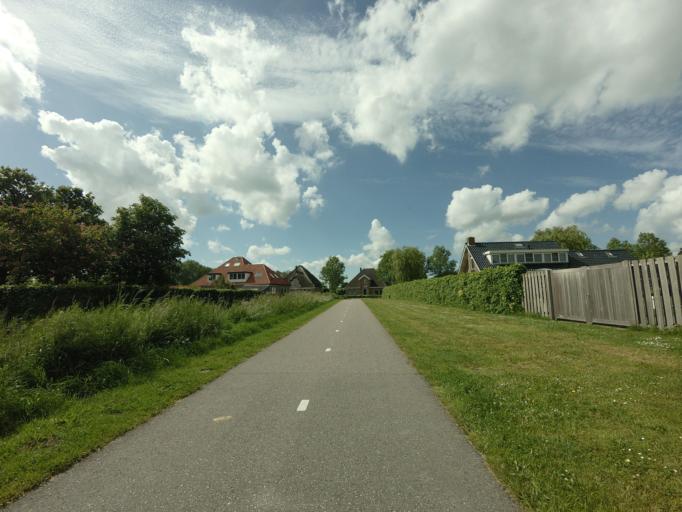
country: NL
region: North Holland
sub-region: Gemeente Hoorn
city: Hoorn
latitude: 52.6857
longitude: 5.0524
